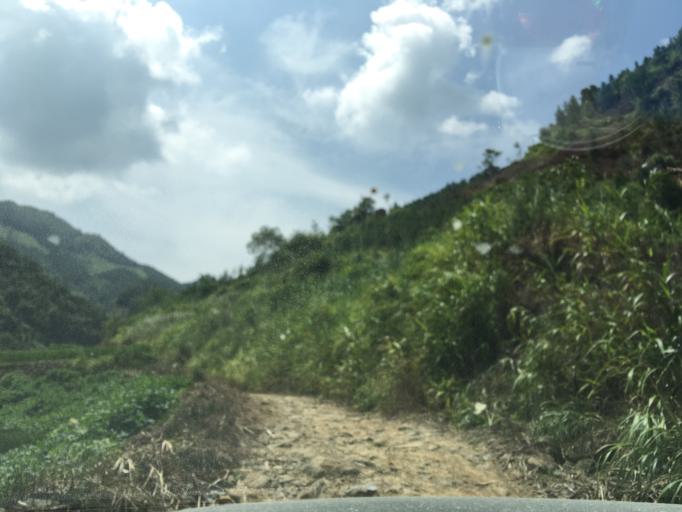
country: CN
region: Guangxi Zhuangzu Zizhiqu
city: Xinzhou
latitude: 24.9536
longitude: 105.7908
